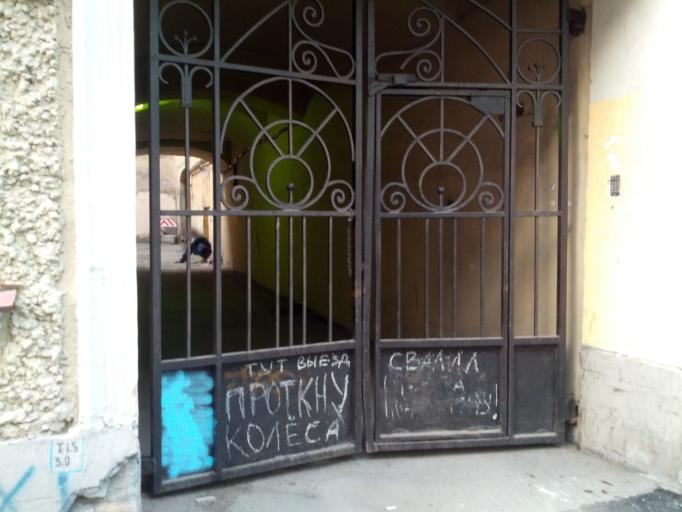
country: RU
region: St.-Petersburg
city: Saint Petersburg
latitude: 59.9281
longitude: 30.3264
